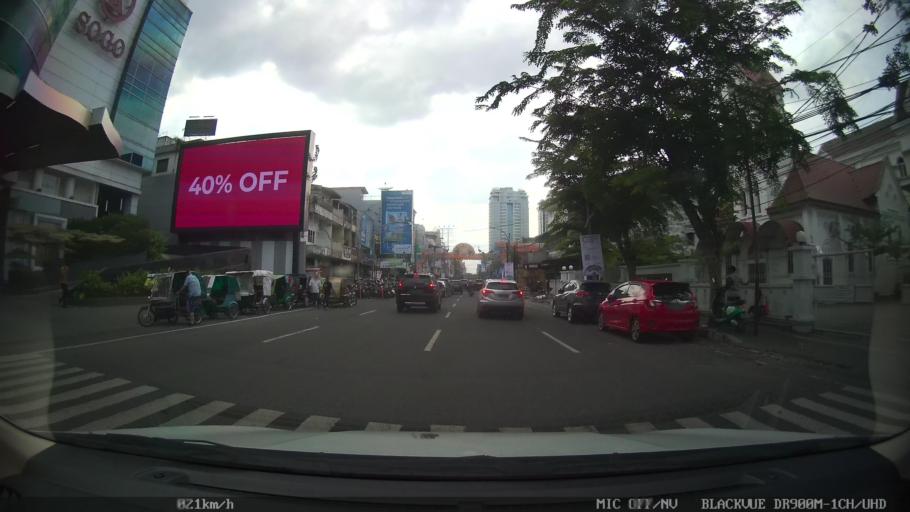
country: ID
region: North Sumatra
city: Medan
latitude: 3.5837
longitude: 98.6719
